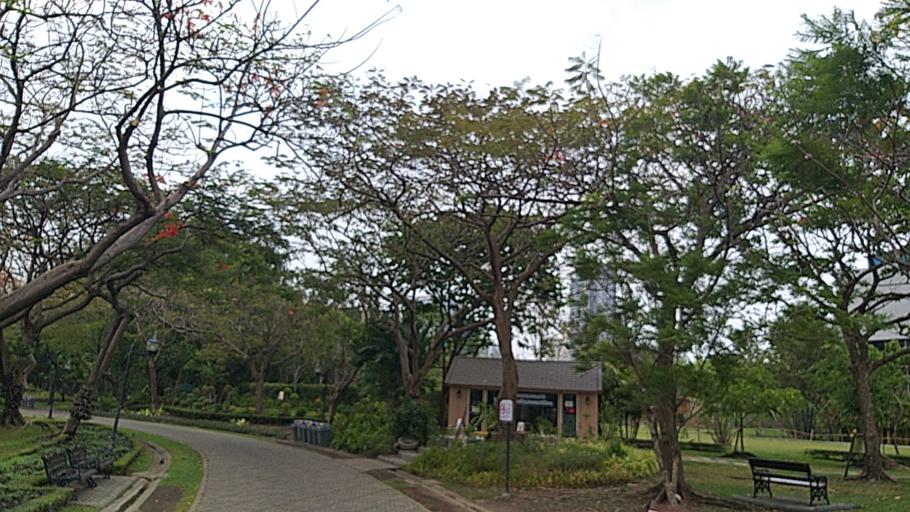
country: TH
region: Bangkok
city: Bang Sue
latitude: 13.8039
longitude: 100.5500
